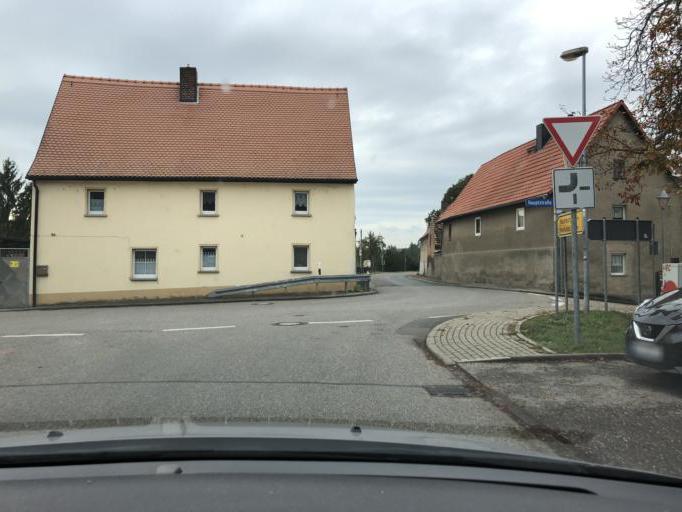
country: DE
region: Saxony-Anhalt
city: Uichteritz
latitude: 51.2152
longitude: 11.9406
